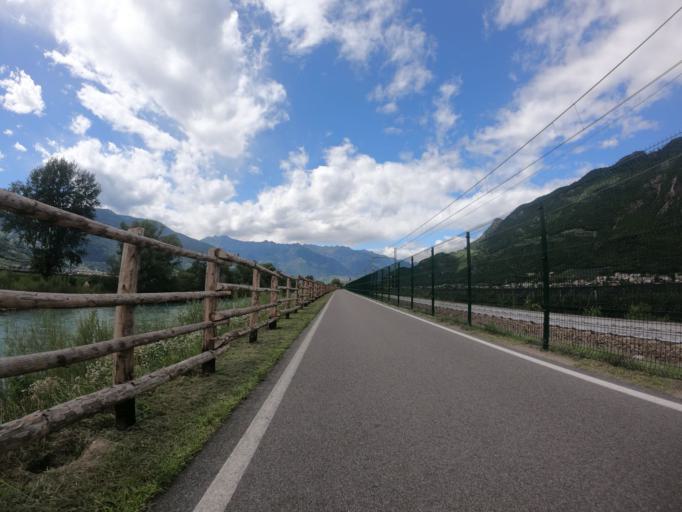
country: IT
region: Trentino-Alto Adige
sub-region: Bolzano
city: Postal
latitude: 46.5993
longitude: 11.1863
